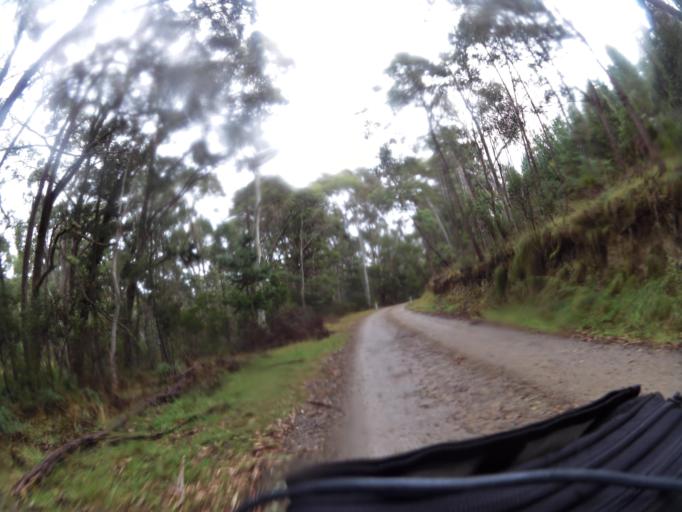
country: AU
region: New South Wales
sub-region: Greater Hume Shire
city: Holbrook
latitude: -36.1952
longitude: 147.5339
